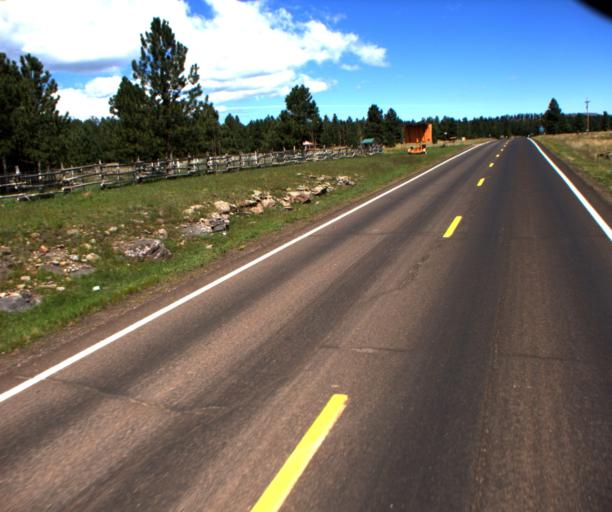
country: US
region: Arizona
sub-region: Apache County
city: Eagar
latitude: 34.0283
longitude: -109.4506
